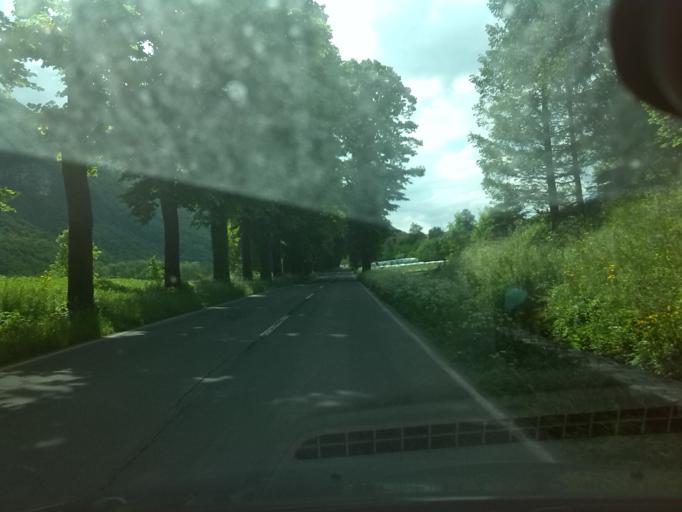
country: SI
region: Kobarid
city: Kobarid
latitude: 46.2460
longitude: 13.5342
